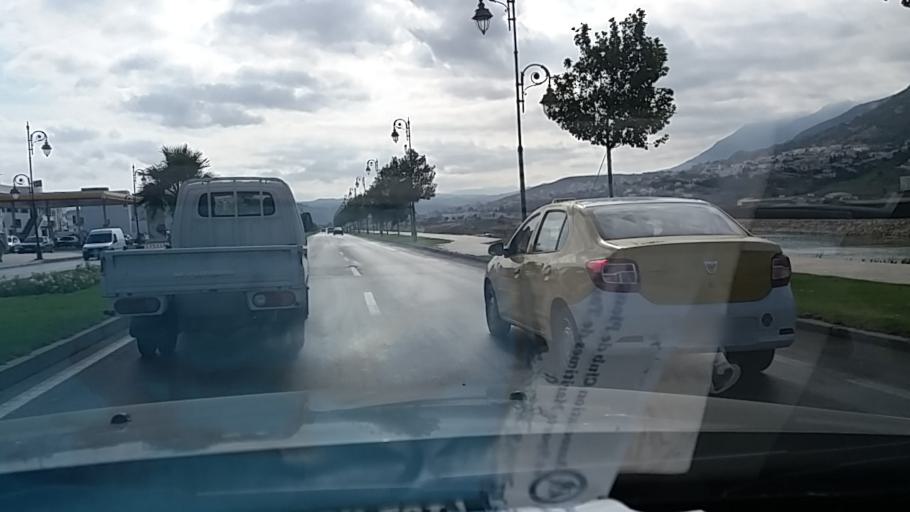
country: MA
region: Tanger-Tetouan
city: Tetouan
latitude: 35.5646
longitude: -5.3802
